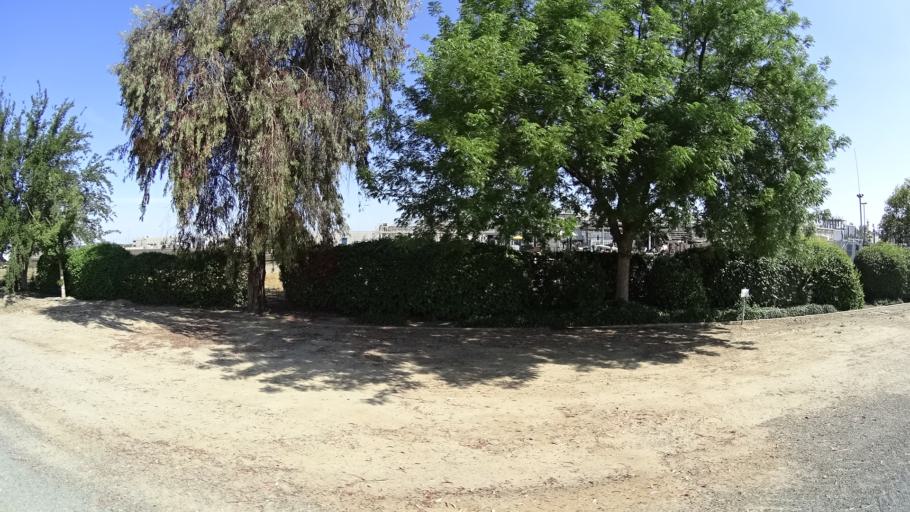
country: US
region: California
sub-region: Kings County
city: Home Garden
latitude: 36.2549
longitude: -119.6496
